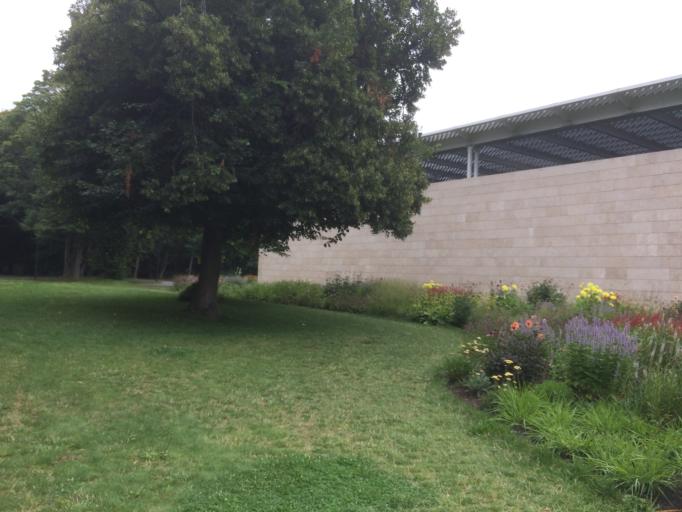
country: NL
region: South Holland
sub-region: Gemeente Leidschendam-Voorburg
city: Voorburg
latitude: 52.1196
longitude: 4.3473
